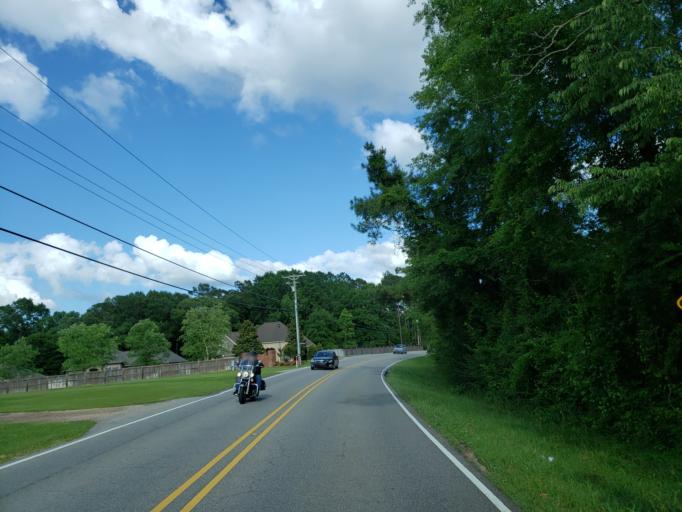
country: US
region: Mississippi
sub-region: Lamar County
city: West Hattiesburg
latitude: 31.2886
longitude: -89.4432
